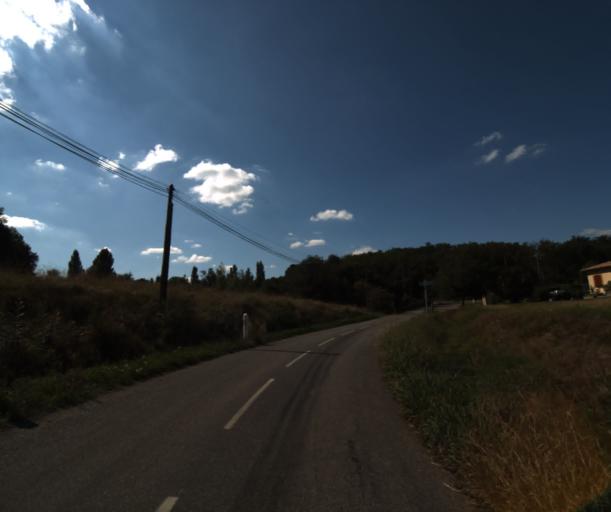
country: FR
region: Midi-Pyrenees
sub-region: Departement de la Haute-Garonne
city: Fonsorbes
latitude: 43.4995
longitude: 1.2201
